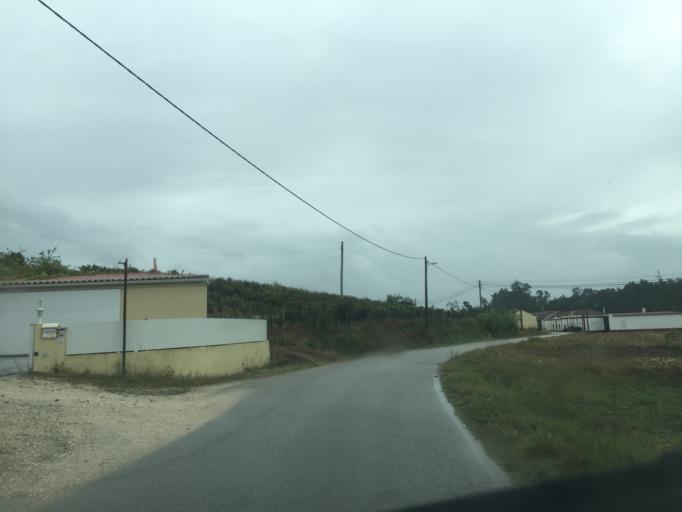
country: PT
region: Coimbra
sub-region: Figueira da Foz
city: Lavos
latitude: 40.0668
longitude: -8.7804
